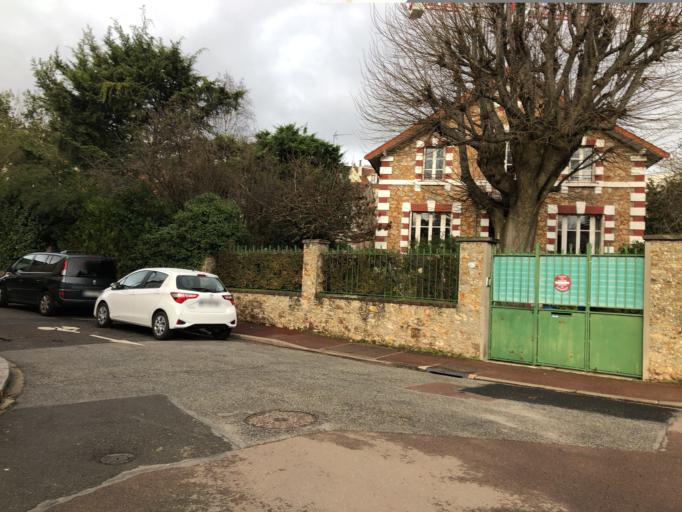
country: FR
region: Ile-de-France
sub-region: Departement des Hauts-de-Seine
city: Chaville
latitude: 48.8052
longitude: 2.1857
